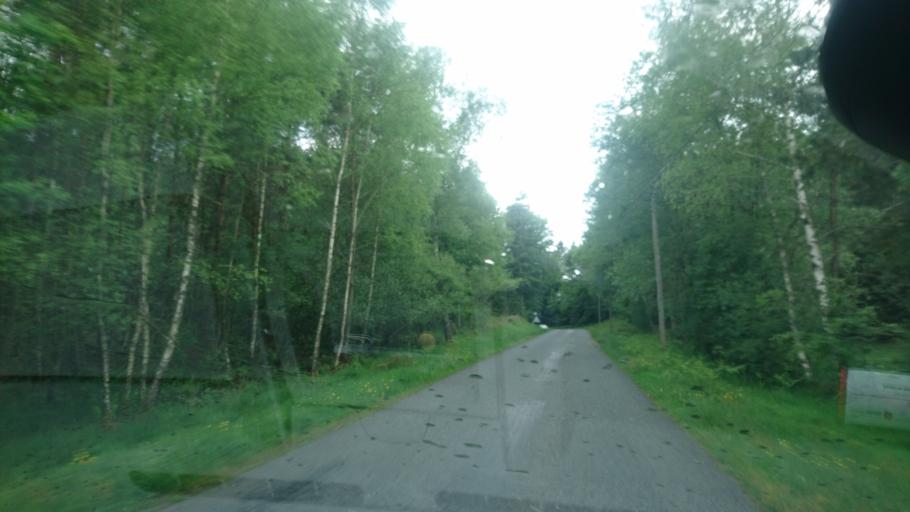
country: FR
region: Limousin
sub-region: Departement de la Haute-Vienne
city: Peyrat-le-Chateau
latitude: 45.8312
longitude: 1.8513
